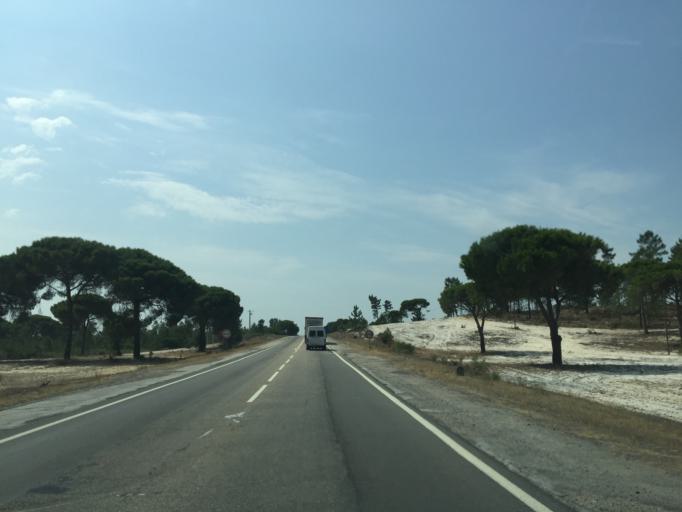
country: PT
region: Setubal
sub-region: Grandola
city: Grandola
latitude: 38.2587
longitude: -8.5454
